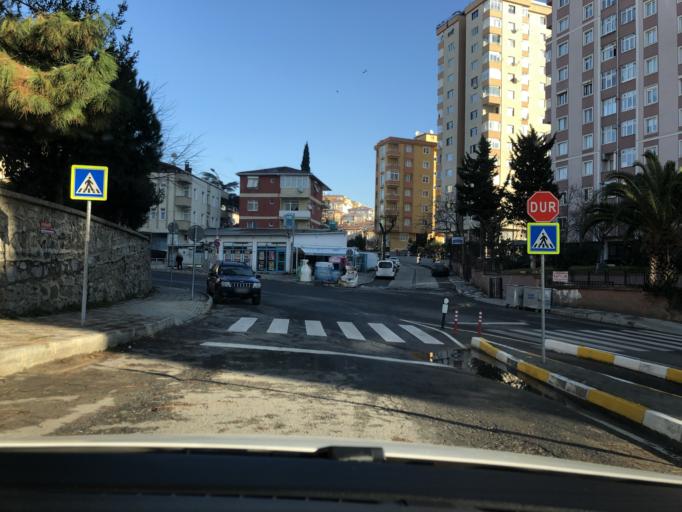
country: TR
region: Istanbul
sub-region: Atasehir
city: Atasehir
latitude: 40.9703
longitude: 29.1196
